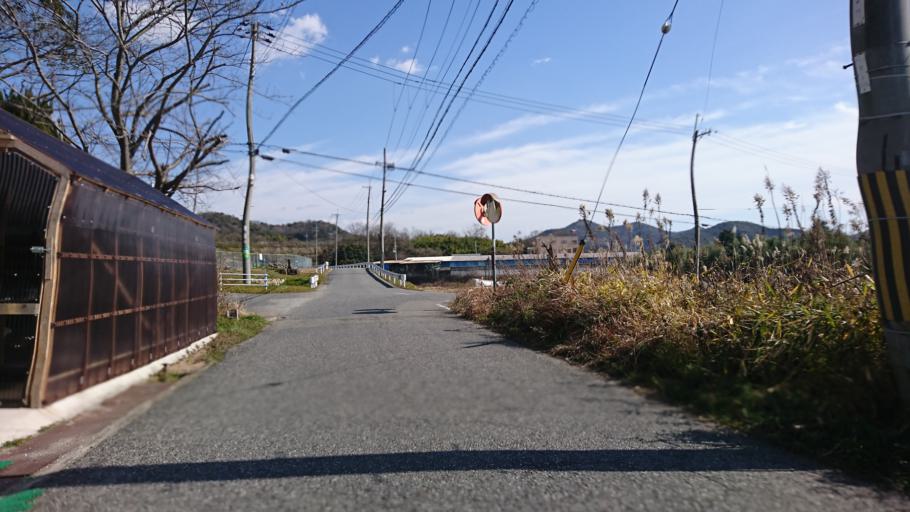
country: JP
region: Hyogo
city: Kakogawacho-honmachi
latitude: 34.8207
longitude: 134.8293
